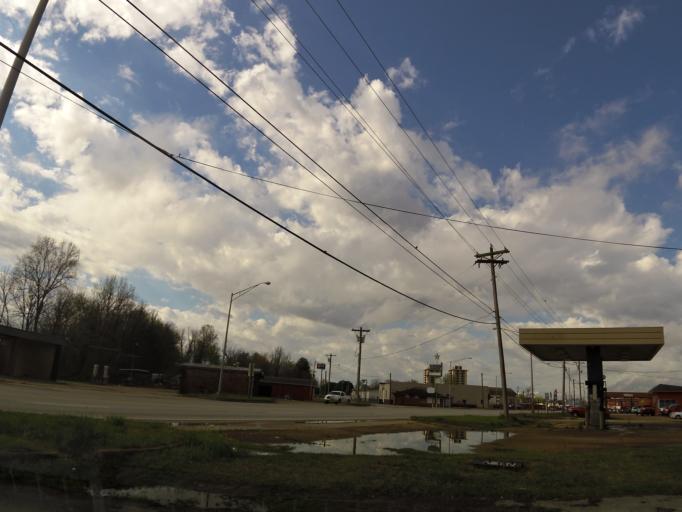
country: US
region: Missouri
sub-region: Butler County
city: Poplar Bluff
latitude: 36.7606
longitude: -90.3811
